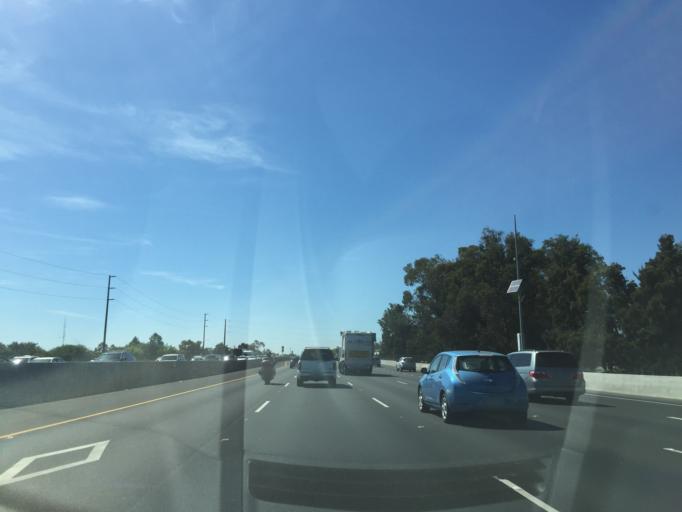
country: US
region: California
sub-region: Santa Clara County
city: Palo Alto
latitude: 37.4417
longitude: -122.1156
